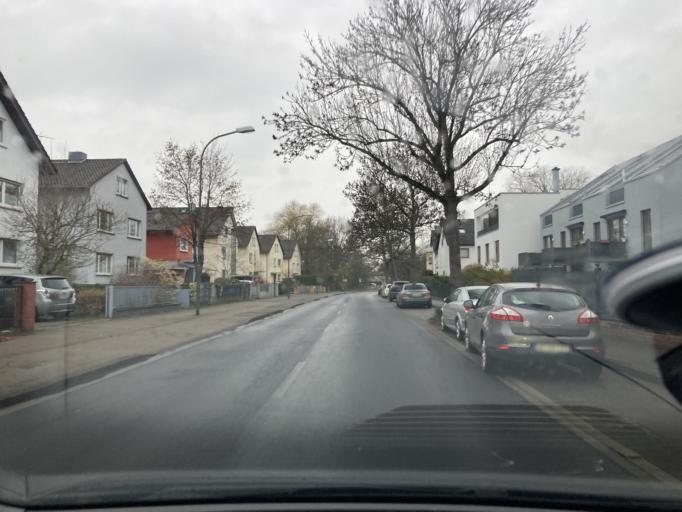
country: DE
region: Hesse
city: Heusenstamm
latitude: 50.0841
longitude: 8.8083
